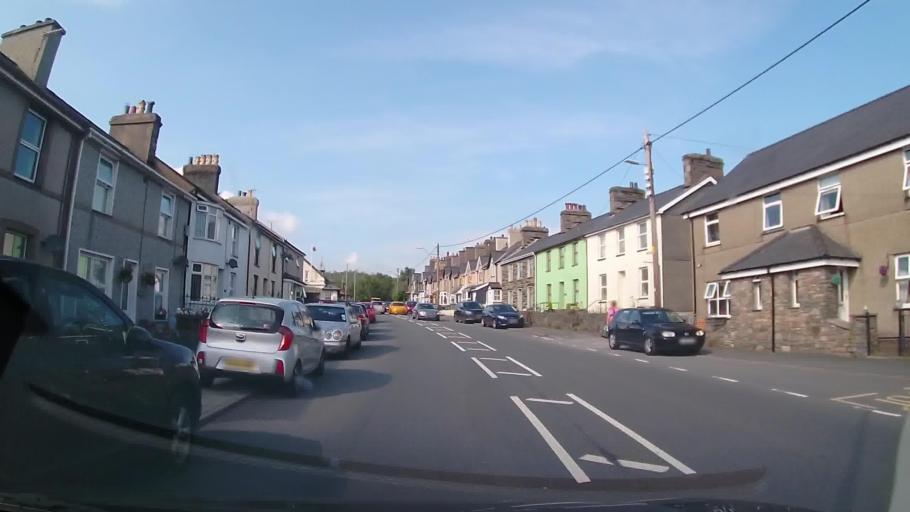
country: GB
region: Wales
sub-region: Gwynedd
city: Penrhyndeudraeth
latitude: 52.9299
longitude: -4.0662
